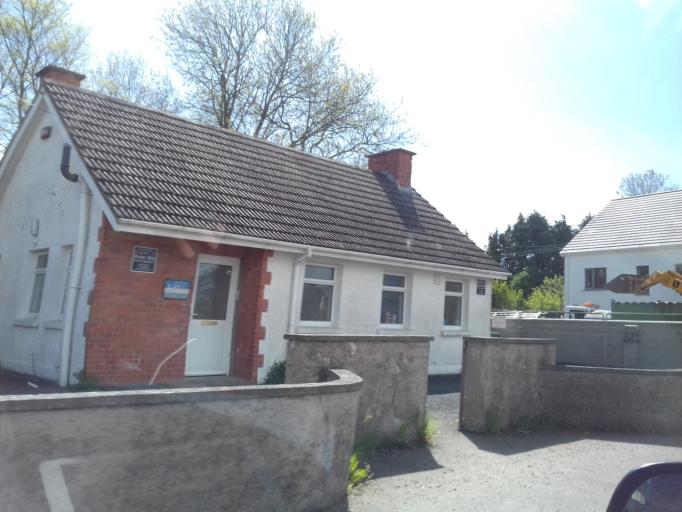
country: IE
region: Leinster
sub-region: Loch Garman
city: Castlebridge
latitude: 52.3810
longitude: -6.4503
